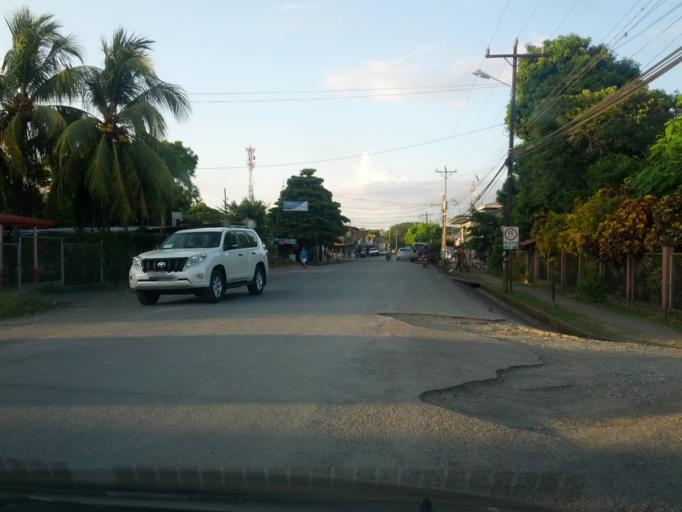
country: CR
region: Puntarenas
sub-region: Canton de Golfito
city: Golfito
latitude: 8.5359
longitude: -83.3058
